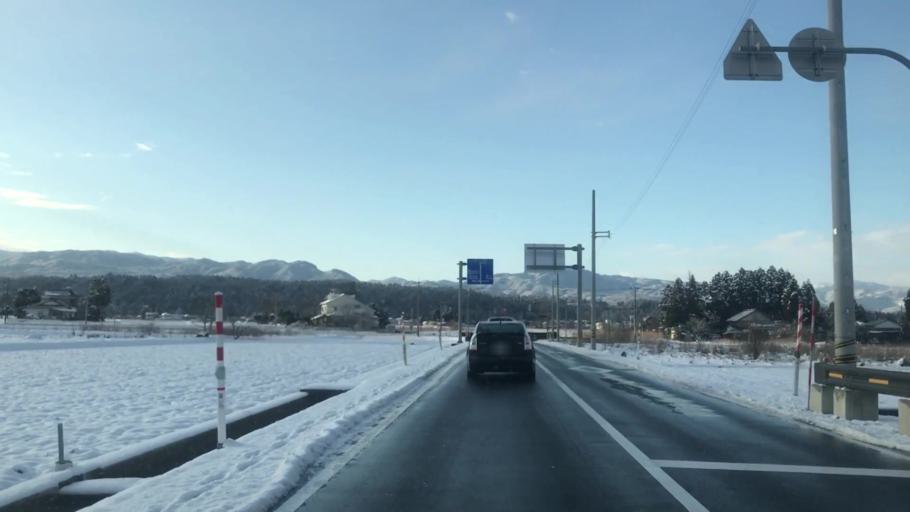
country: JP
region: Toyama
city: Toyama-shi
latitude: 36.6165
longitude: 137.2865
